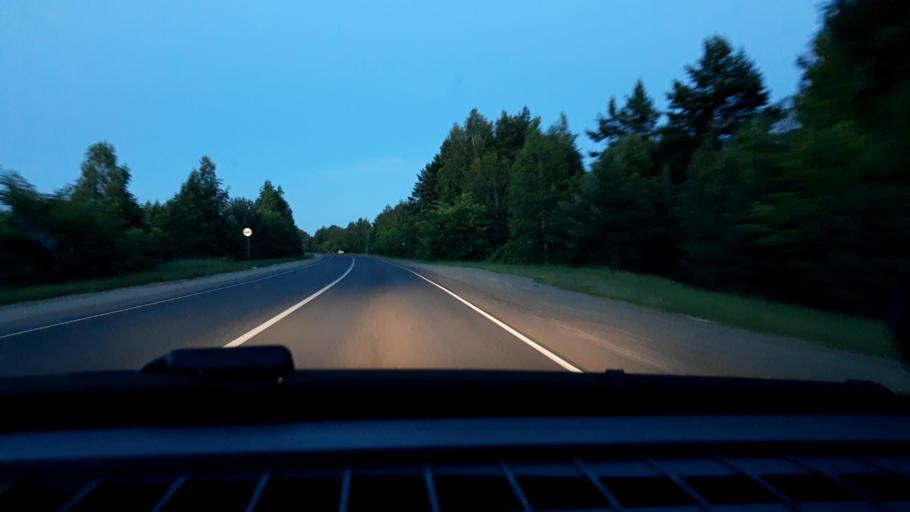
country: RU
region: Nizjnij Novgorod
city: Gidrotorf
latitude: 56.5591
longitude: 43.4983
